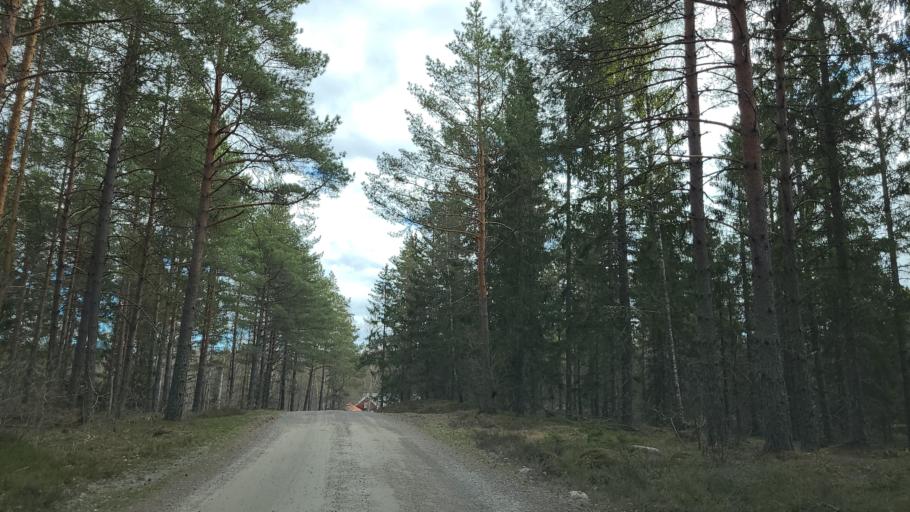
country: SE
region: OEstergoetland
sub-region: Norrkopings Kommun
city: Krokek
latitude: 58.6854
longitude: 16.4195
